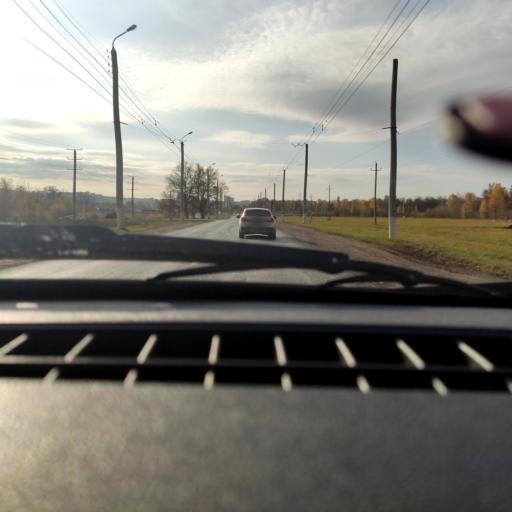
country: RU
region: Bashkortostan
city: Ufa
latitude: 54.7817
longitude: 55.9476
